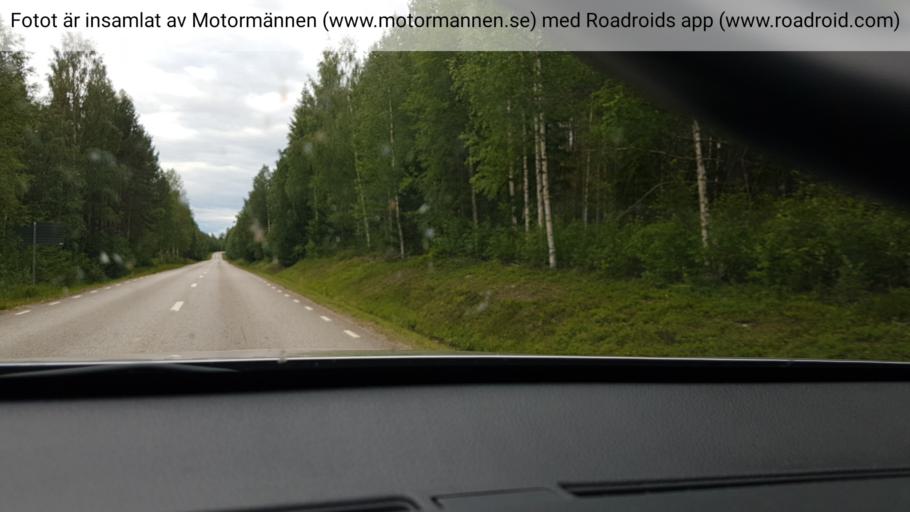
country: NO
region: Hedmark
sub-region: Trysil
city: Innbygda
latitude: 61.0390
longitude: 12.5861
